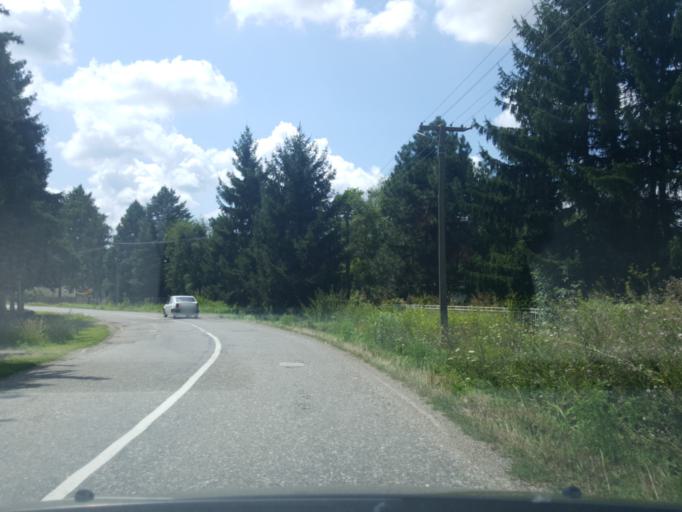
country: RS
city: Zminjak
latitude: 44.7392
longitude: 19.4646
